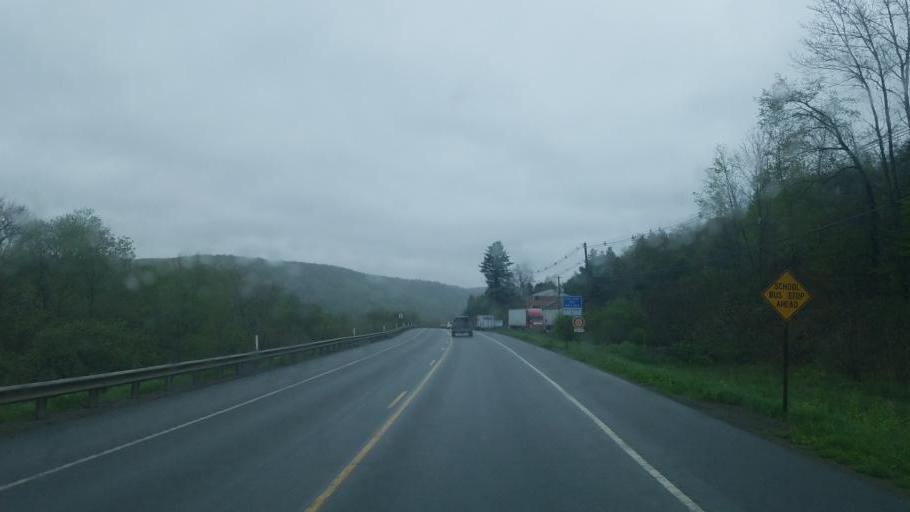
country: US
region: Pennsylvania
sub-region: McKean County
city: Port Allegany
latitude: 41.8031
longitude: -78.2700
